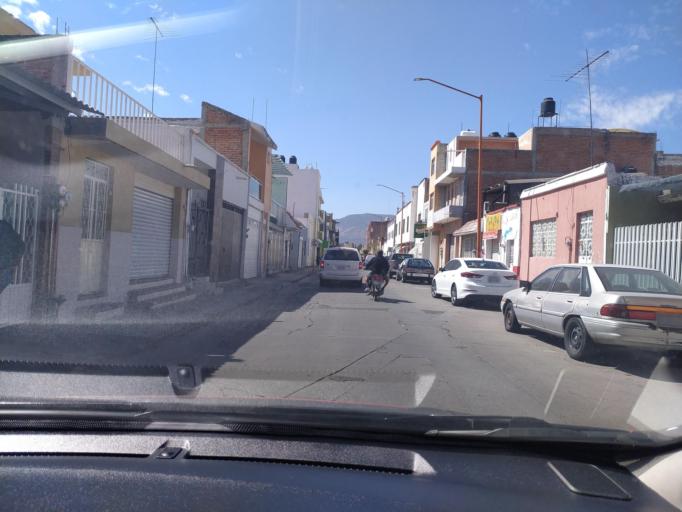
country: LA
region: Oudomxai
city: Muang La
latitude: 21.0218
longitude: 101.8573
